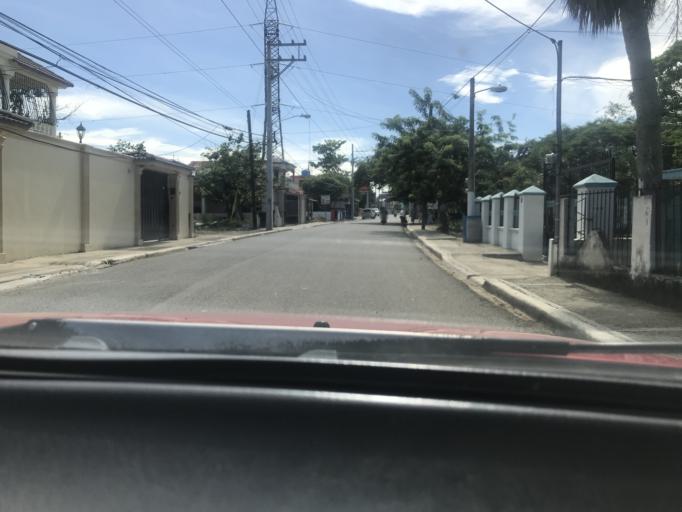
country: DO
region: Santiago
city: Licey al Medio
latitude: 19.4057
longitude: -70.6281
